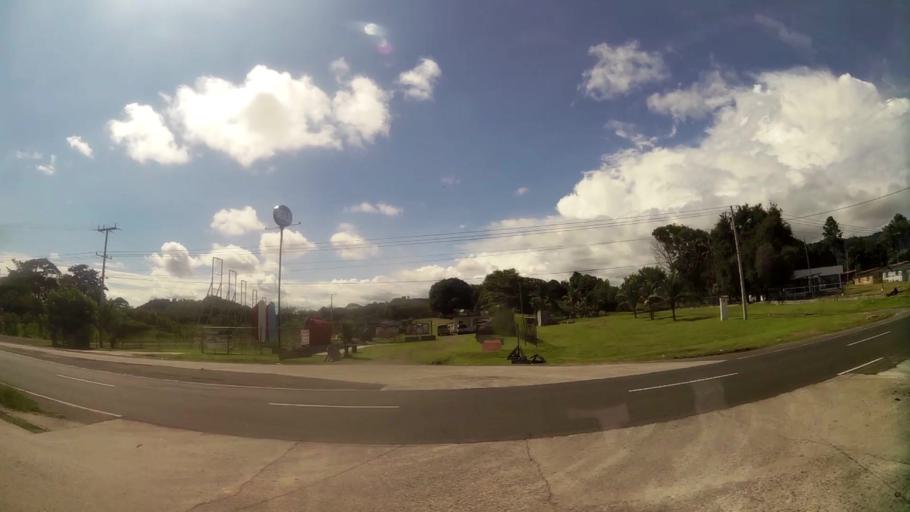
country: PA
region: Panama
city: Bejuco
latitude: 8.6204
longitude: -79.8807
